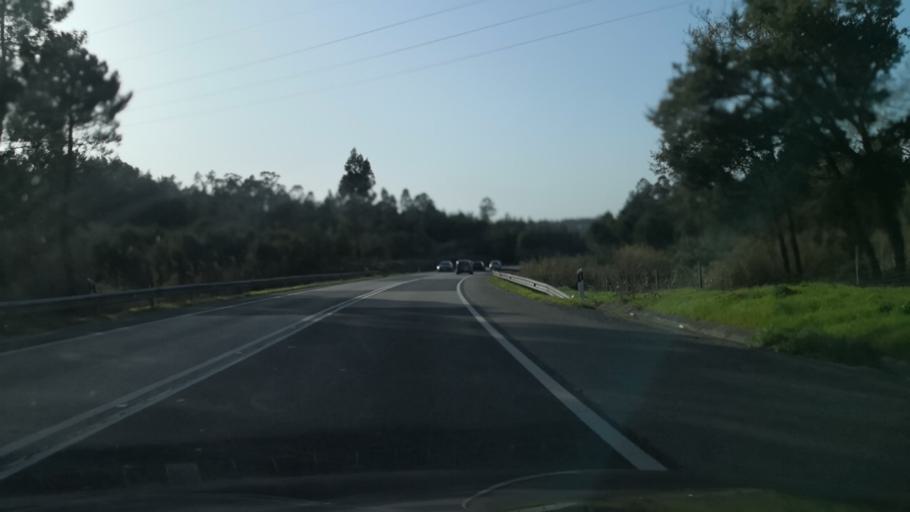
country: PT
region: Leiria
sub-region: Leiria
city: Leiria
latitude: 39.7431
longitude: -8.8417
